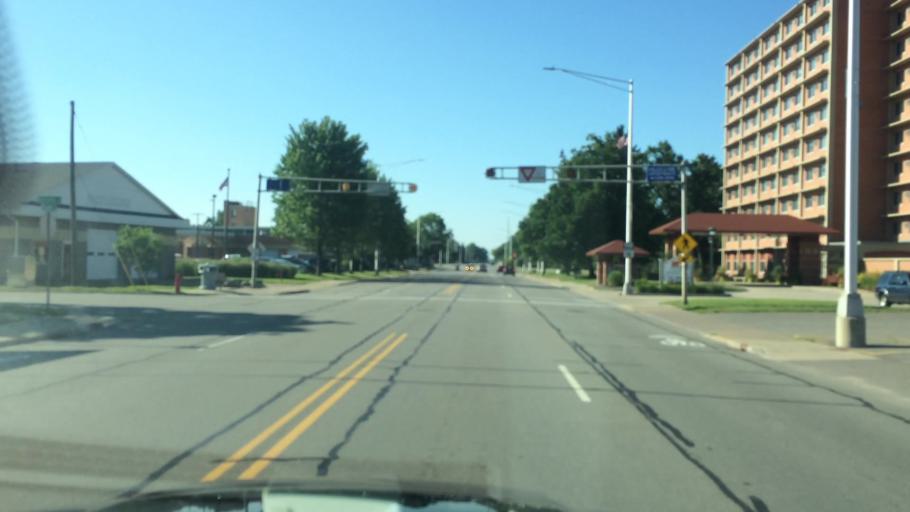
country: US
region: Wisconsin
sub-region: Marathon County
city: Wausau
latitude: 44.9531
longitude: -89.6233
